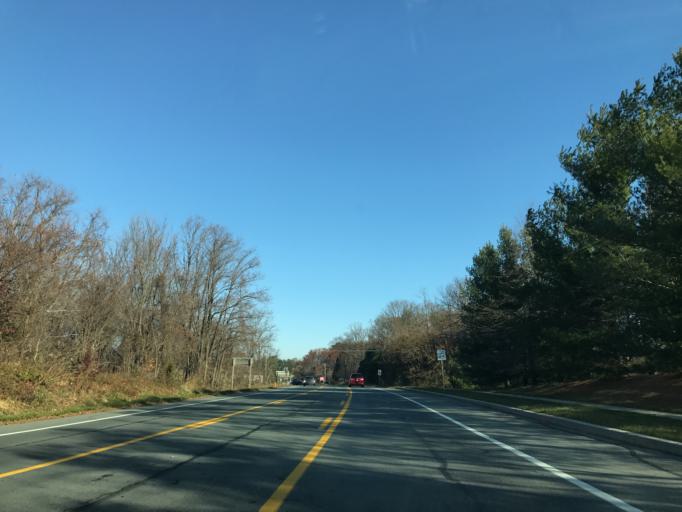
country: US
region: Maryland
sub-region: Howard County
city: Ellicott City
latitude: 39.2306
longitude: -76.7994
